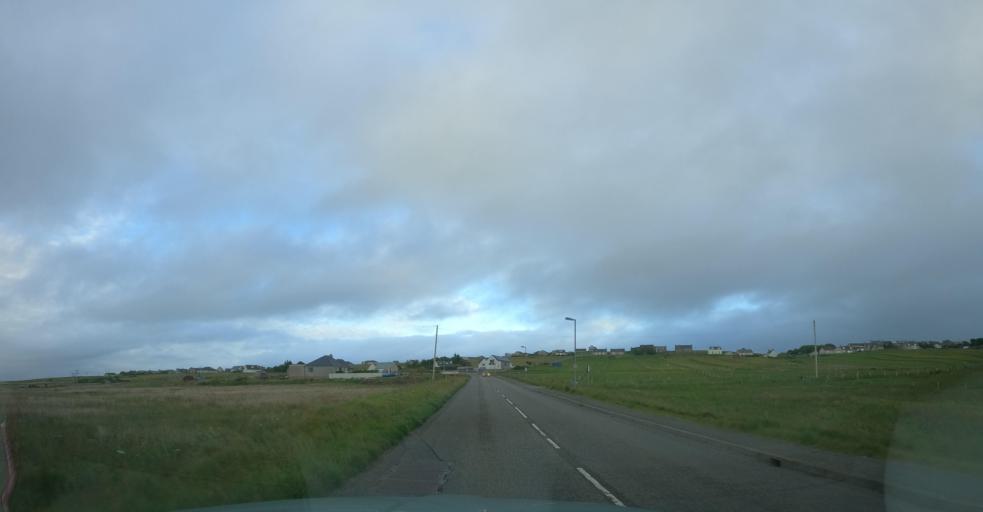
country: GB
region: Scotland
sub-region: Eilean Siar
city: Stornoway
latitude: 58.2052
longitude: -6.2749
